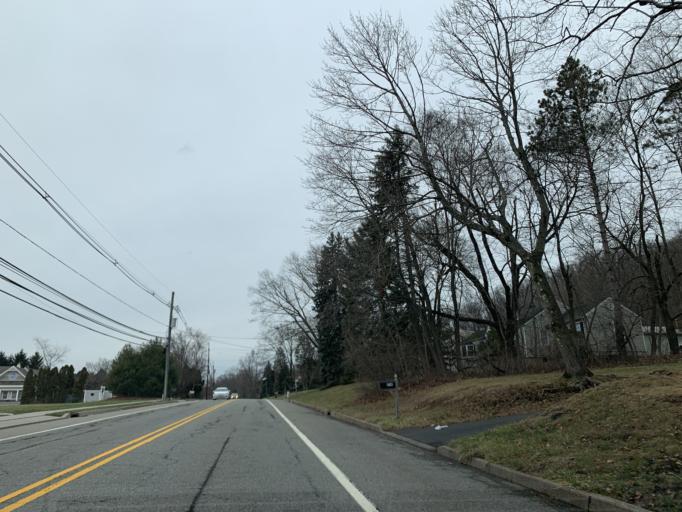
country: US
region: New Jersey
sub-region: Somerset County
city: Martinsville
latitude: 40.6104
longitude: -74.5760
